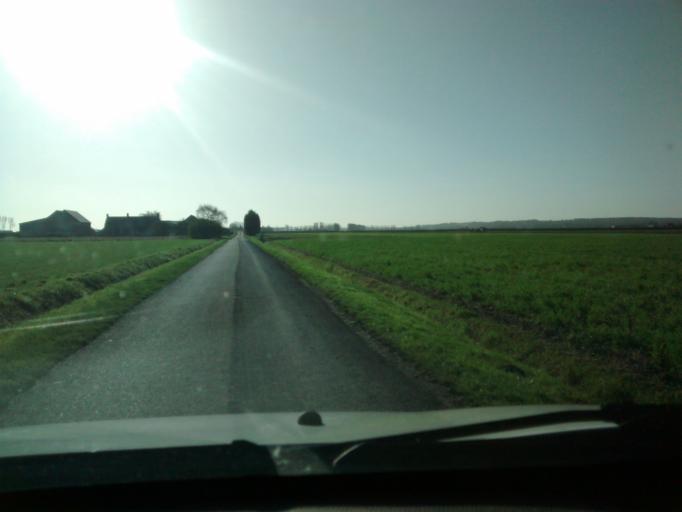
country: FR
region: Brittany
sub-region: Departement d'Ille-et-Vilaine
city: Roz-sur-Couesnon
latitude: 48.6189
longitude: -1.5357
